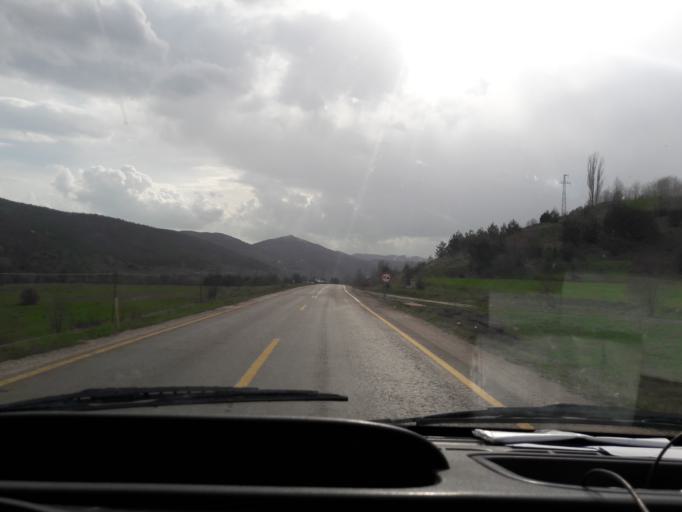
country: TR
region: Giresun
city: Alucra
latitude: 40.2656
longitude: 38.9248
